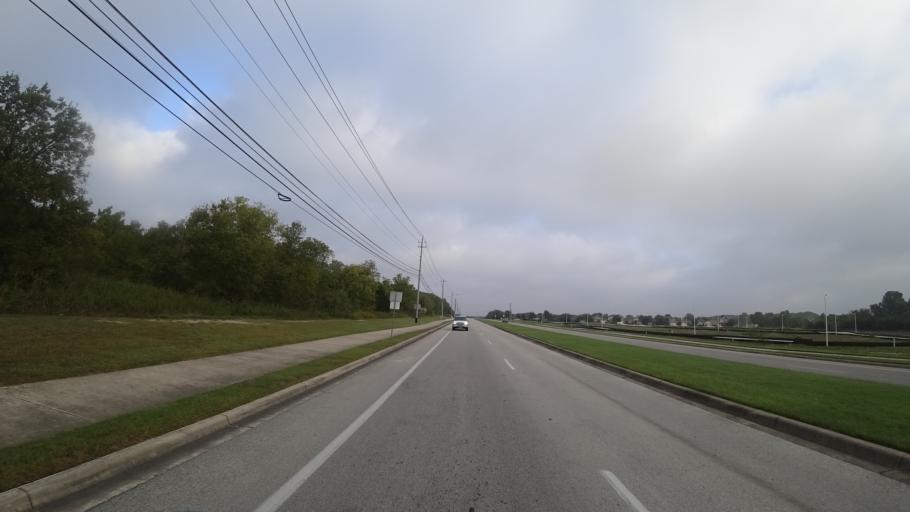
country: US
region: Texas
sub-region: Travis County
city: Pflugerville
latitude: 30.3716
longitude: -97.6554
